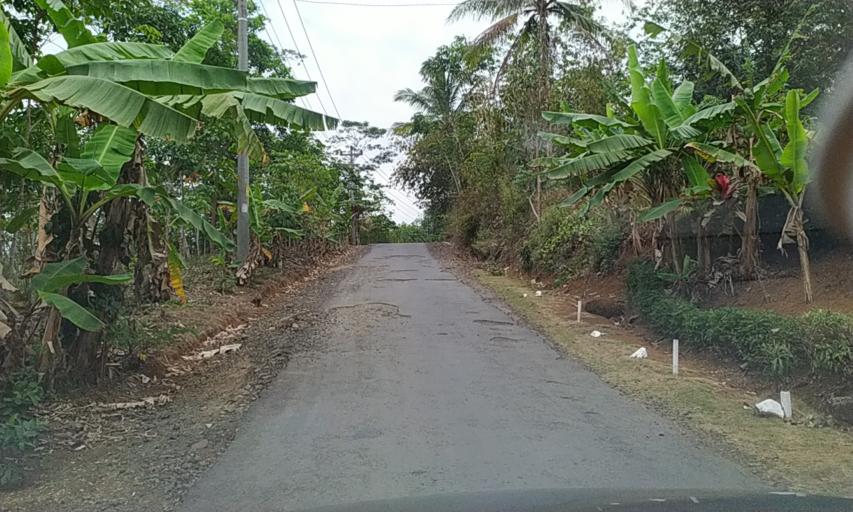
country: ID
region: Central Java
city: Ciwalen
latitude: -7.2890
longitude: 108.6124
